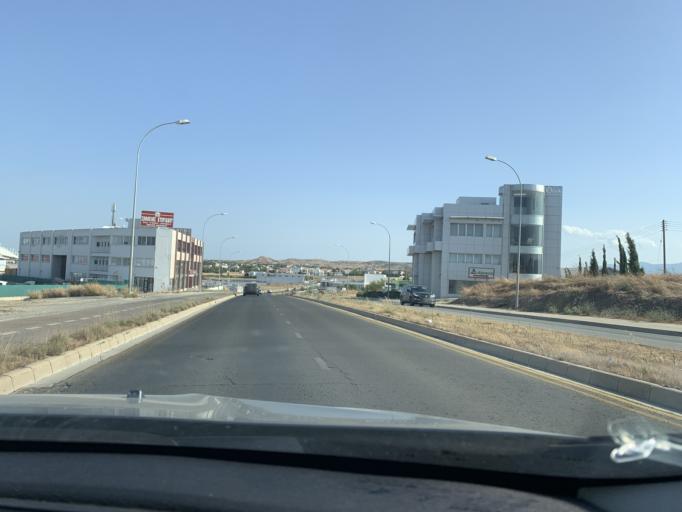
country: CY
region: Lefkosia
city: Nicosia
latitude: 35.1215
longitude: 33.3564
